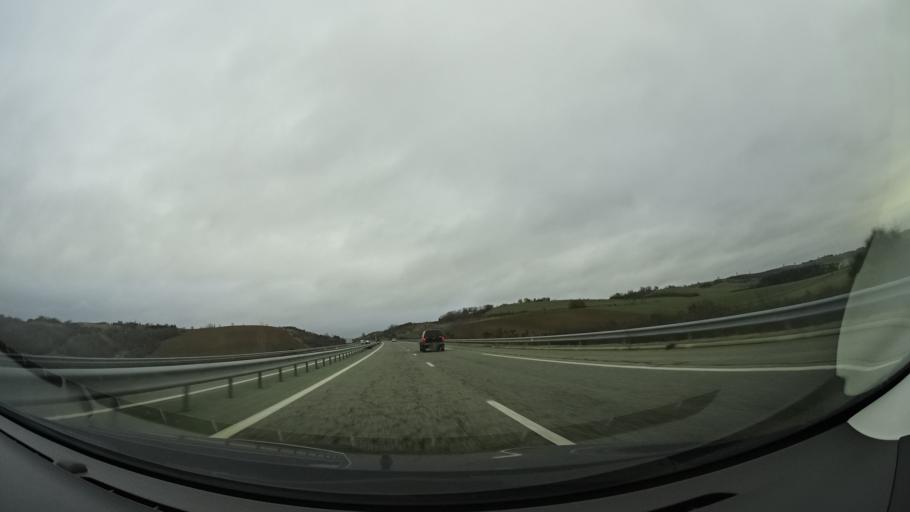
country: FR
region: Midi-Pyrenees
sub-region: Departement de l'Ariege
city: Mazeres
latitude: 43.2693
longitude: 1.6688
